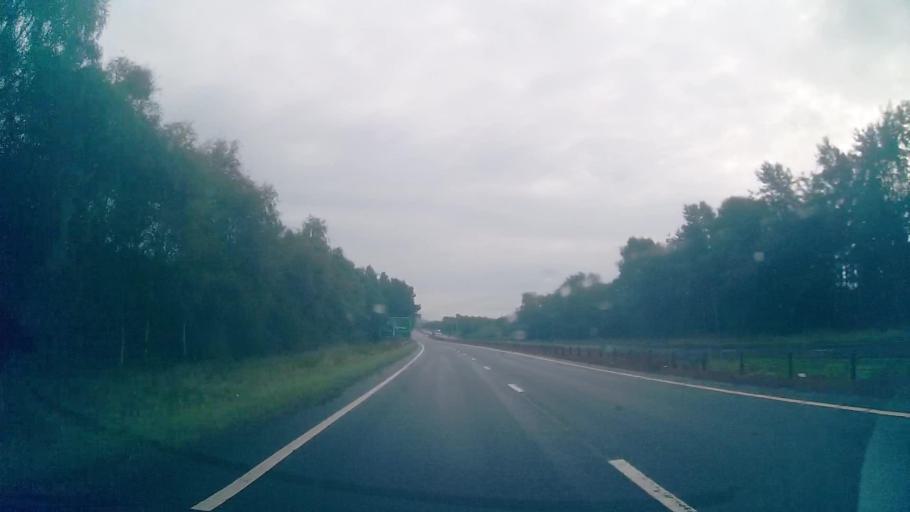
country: GB
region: Scotland
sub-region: Dumfries and Galloway
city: Locharbriggs
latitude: 55.0673
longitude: -3.5278
